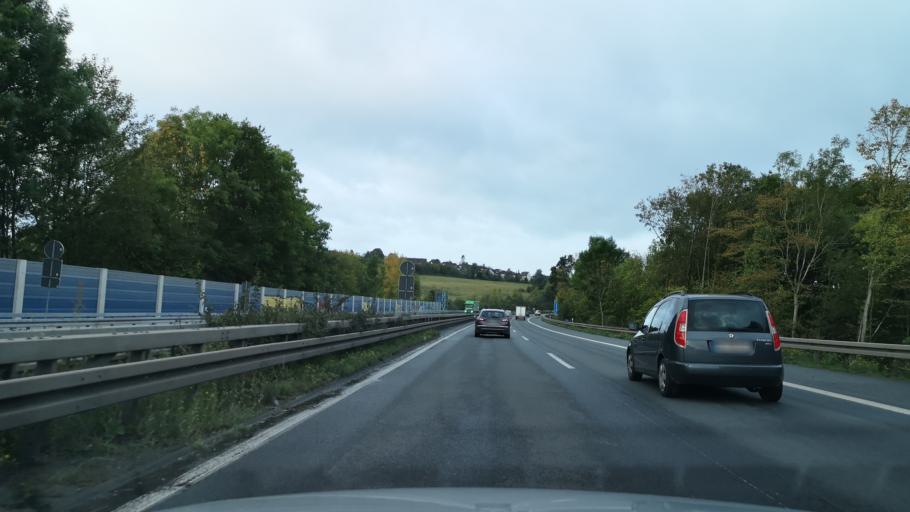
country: DE
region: North Rhine-Westphalia
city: Iserlohn
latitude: 51.3854
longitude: 7.6970
